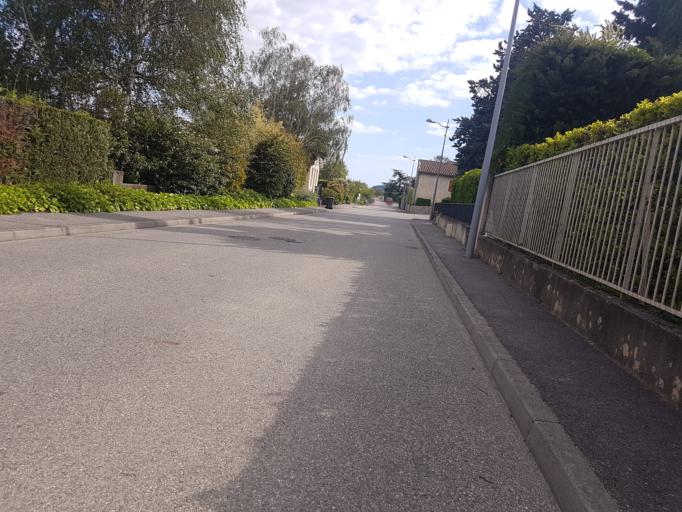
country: FR
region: Rhone-Alpes
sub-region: Departement de l'Ardeche
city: Guilherand-Granges
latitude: 44.9225
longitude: 4.8674
